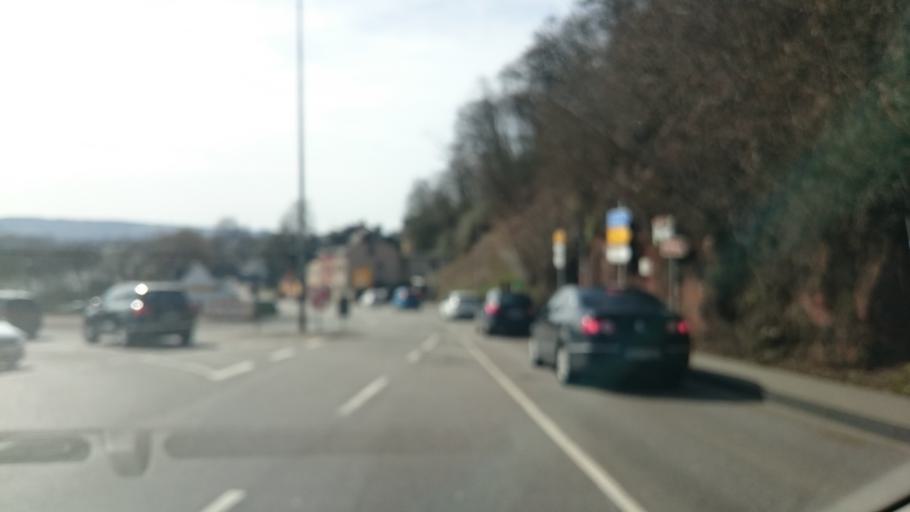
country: DE
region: Rheinland-Pfalz
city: Trier
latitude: 49.7653
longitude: 6.6299
